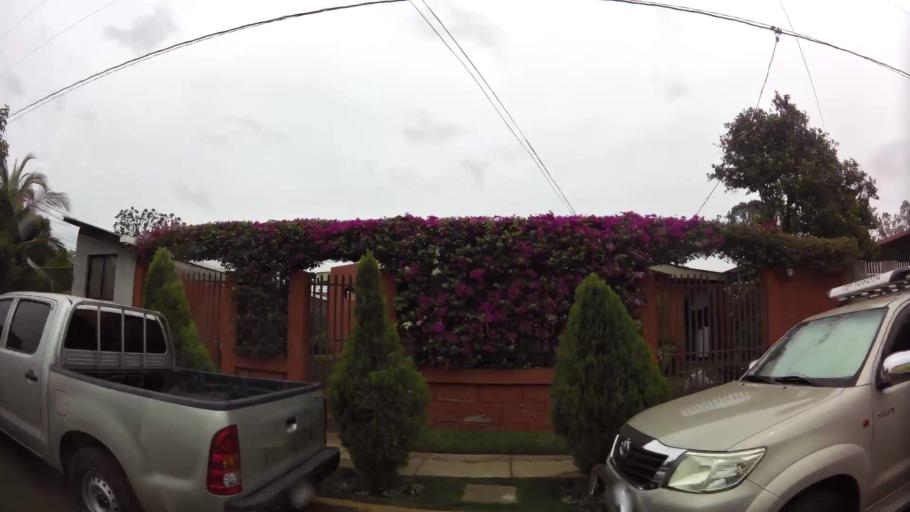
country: NI
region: Masaya
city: Ticuantepe
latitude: 12.0644
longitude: -86.1837
